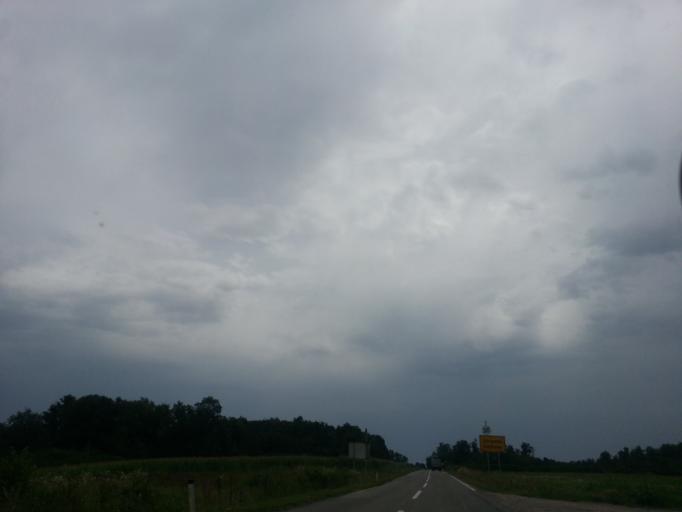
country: BA
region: Republika Srpska
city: Velika Obarska
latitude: 44.8078
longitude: 19.0688
